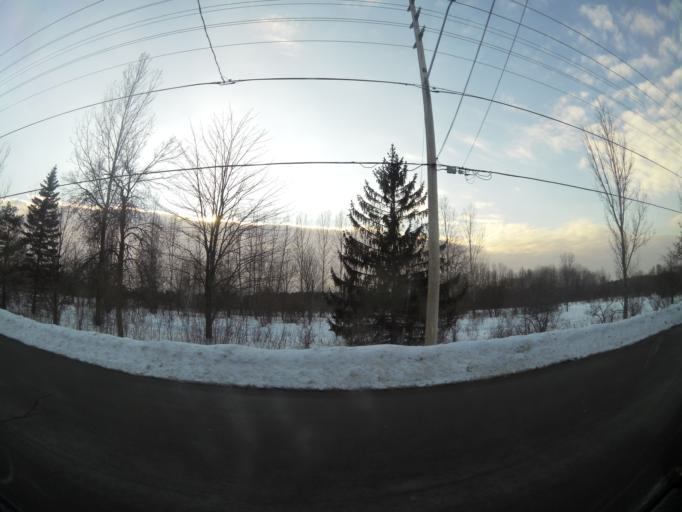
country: CA
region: Ontario
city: Ottawa
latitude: 45.4315
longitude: -75.5746
